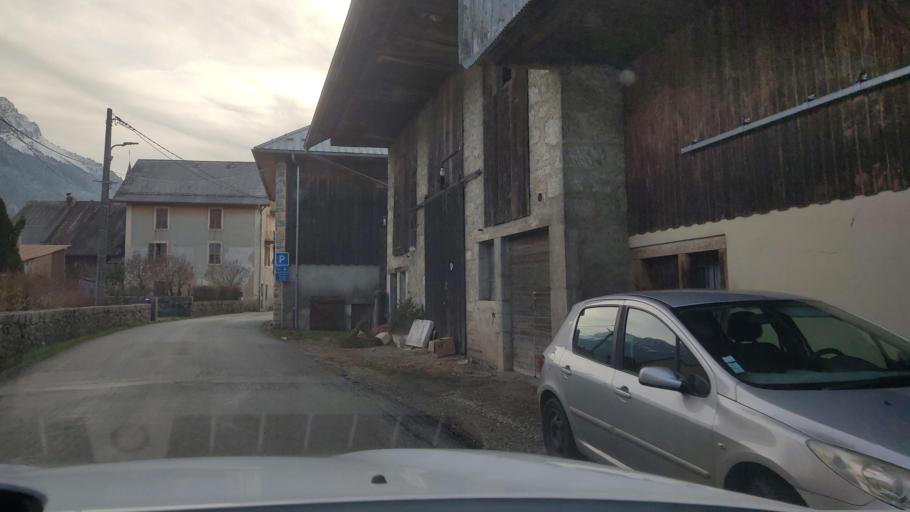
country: FR
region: Rhone-Alpes
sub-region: Departement de la Savoie
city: Gresy-sur-Isere
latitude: 45.6516
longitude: 6.1669
